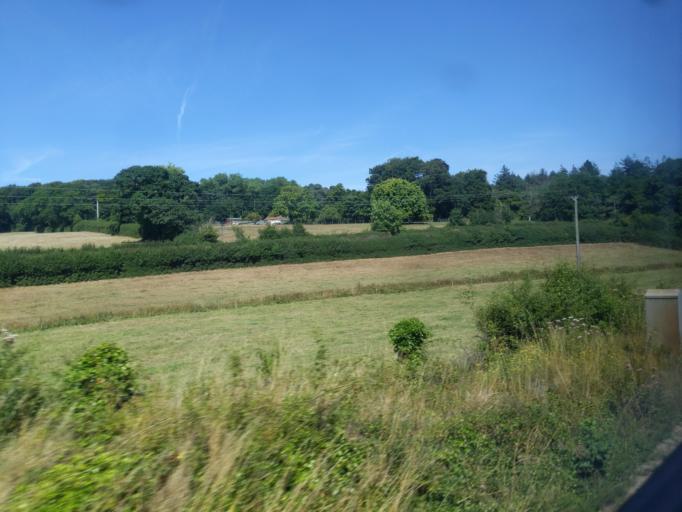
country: GB
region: England
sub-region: Devon
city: Totnes
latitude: 50.4352
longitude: -3.7160
